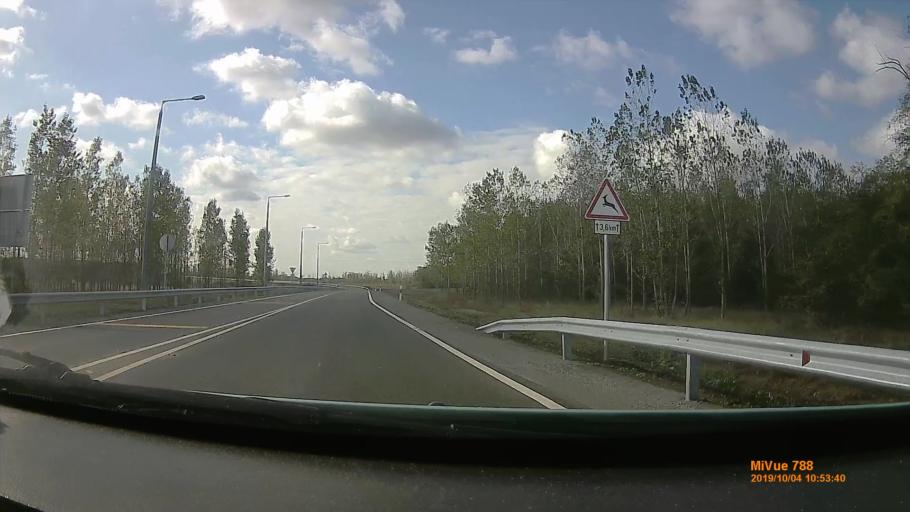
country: HU
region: Szabolcs-Szatmar-Bereg
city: Nyirtelek
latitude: 47.9871
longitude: 21.6697
